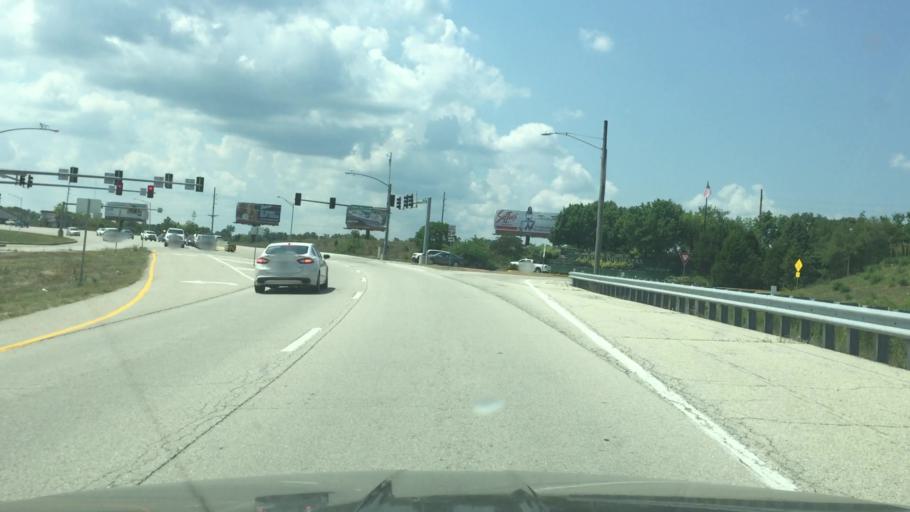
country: US
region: Missouri
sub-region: Miller County
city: Lake Ozark
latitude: 38.1763
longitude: -92.6151
